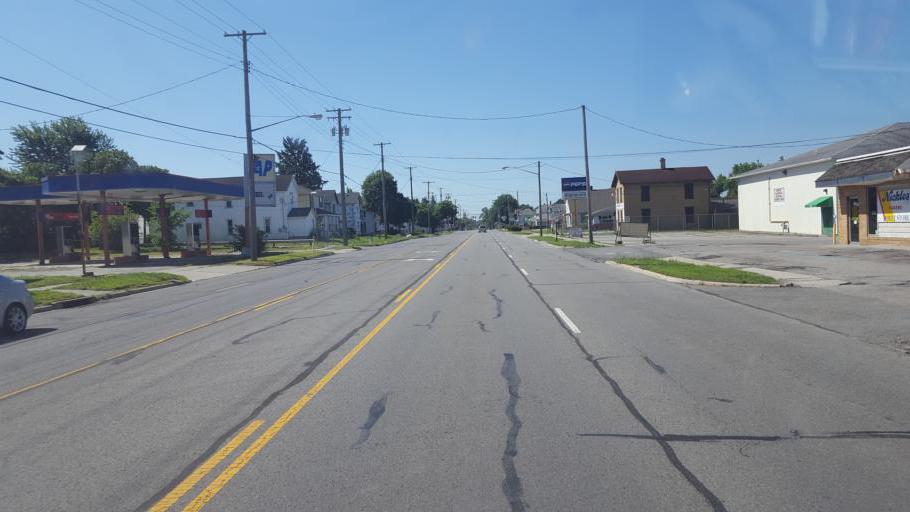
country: US
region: Ohio
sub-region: Marion County
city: Marion
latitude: 40.6030
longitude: -83.1299
